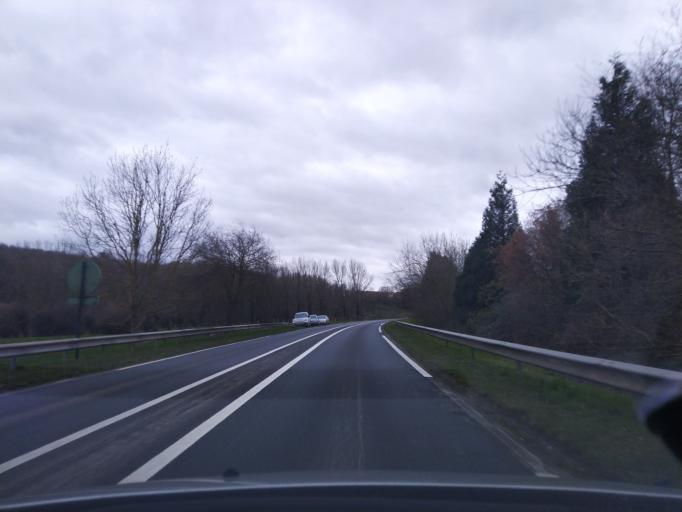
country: FR
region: Nord-Pas-de-Calais
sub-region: Departement du Pas-de-Calais
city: Camblain-Chatelain
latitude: 50.4381
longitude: 2.4549
